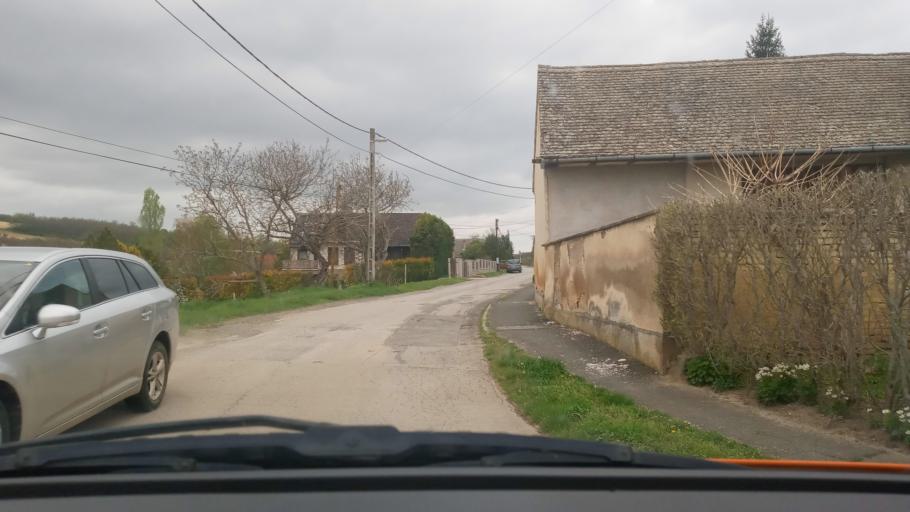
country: HU
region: Baranya
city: Boly
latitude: 46.0061
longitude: 18.5494
